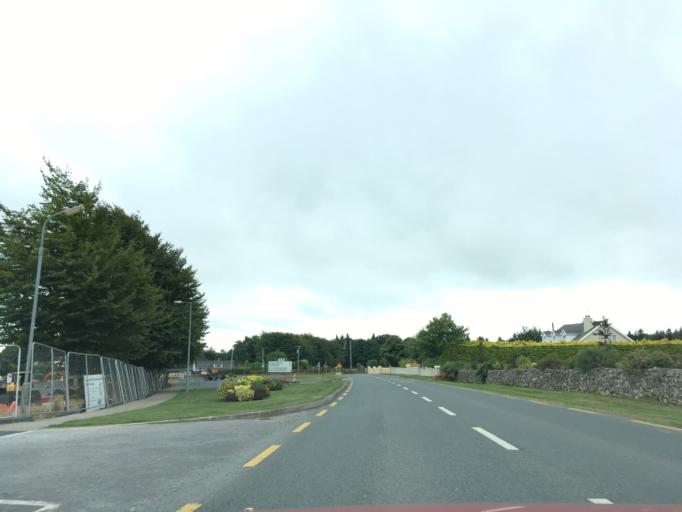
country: IE
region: Munster
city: Cashel
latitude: 52.4675
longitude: -7.8318
